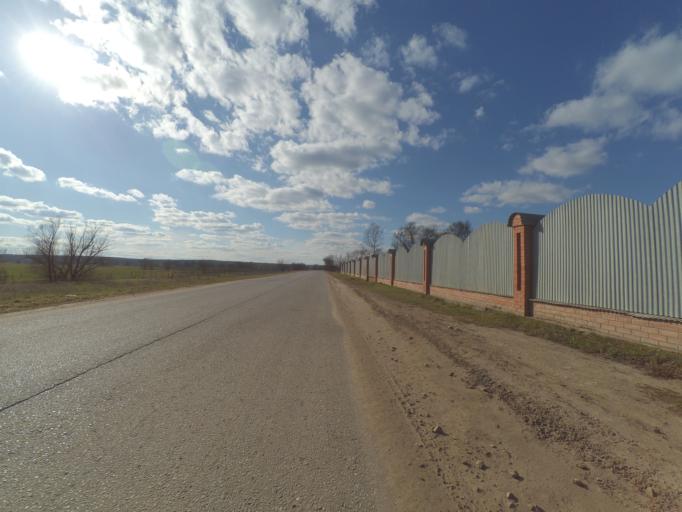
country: RU
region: Moskovskaya
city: Bol'shoye Gryzlovo
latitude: 54.8692
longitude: 37.8408
